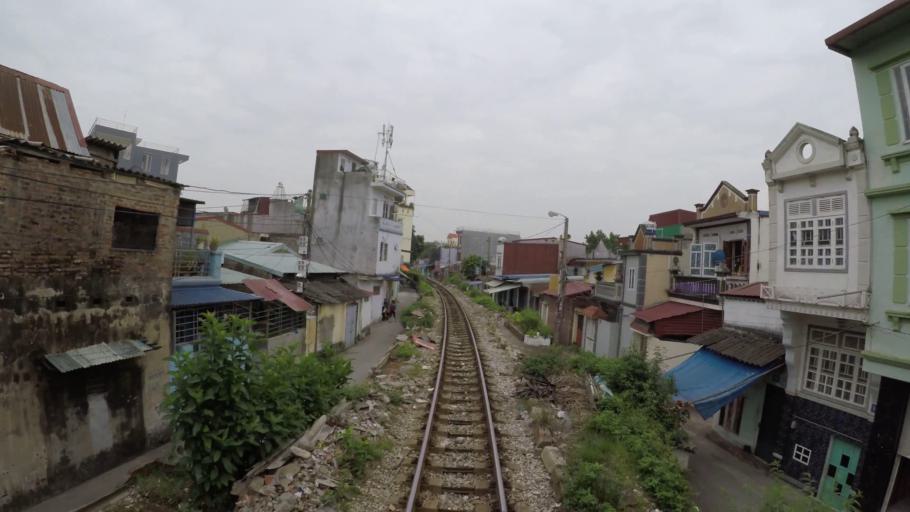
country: VN
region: Hai Phong
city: Haiphong
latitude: 20.8694
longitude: 106.6542
